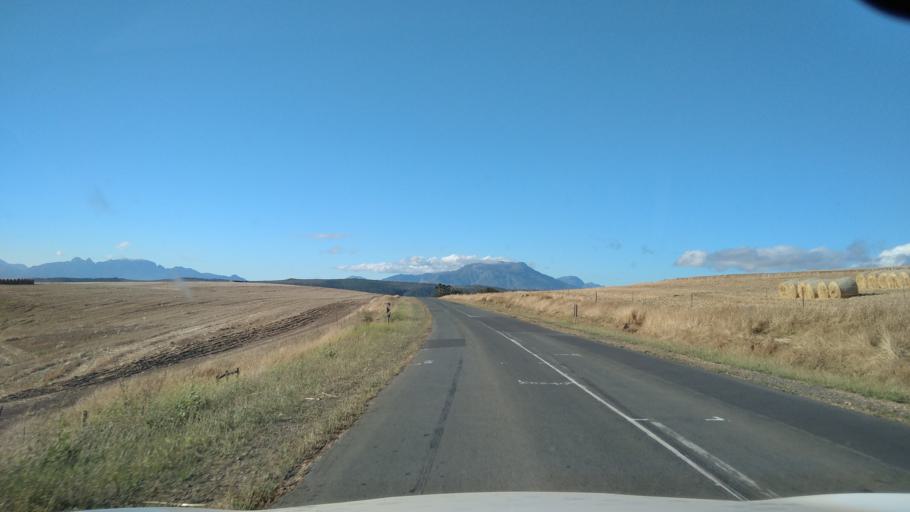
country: ZA
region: Western Cape
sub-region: Overberg District Municipality
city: Caledon
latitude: -34.1474
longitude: 19.2991
